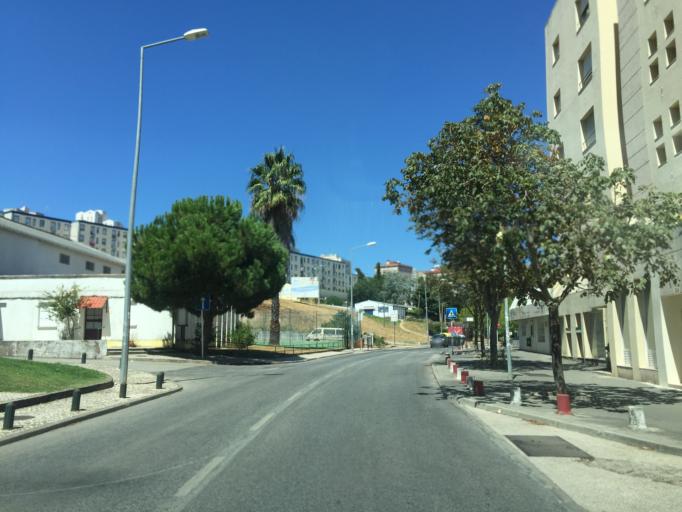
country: PT
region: Lisbon
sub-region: Odivelas
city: Povoa de Santo Adriao
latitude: 38.8104
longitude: -9.1622
